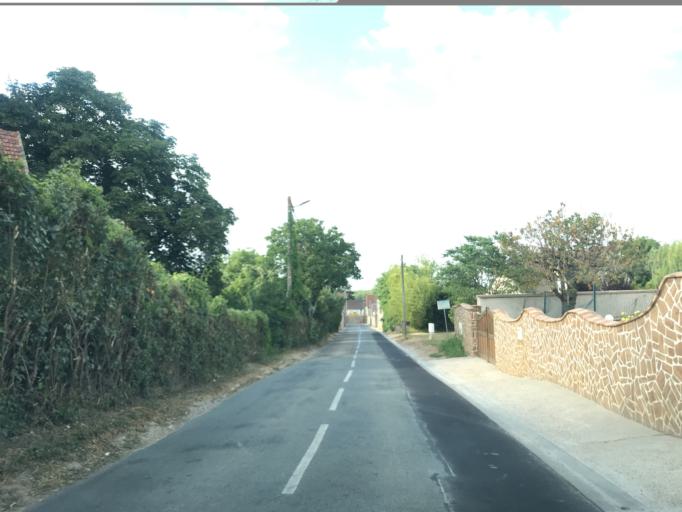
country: FR
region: Haute-Normandie
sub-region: Departement de l'Eure
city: Gasny
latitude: 49.0738
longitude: 1.5920
